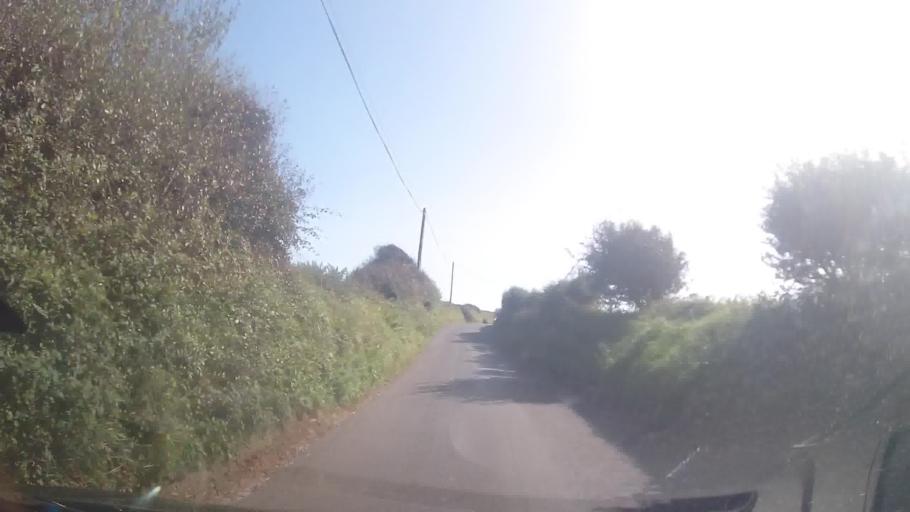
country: GB
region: Wales
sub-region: Pembrokeshire
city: Llanrhian
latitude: 51.9366
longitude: -5.1717
